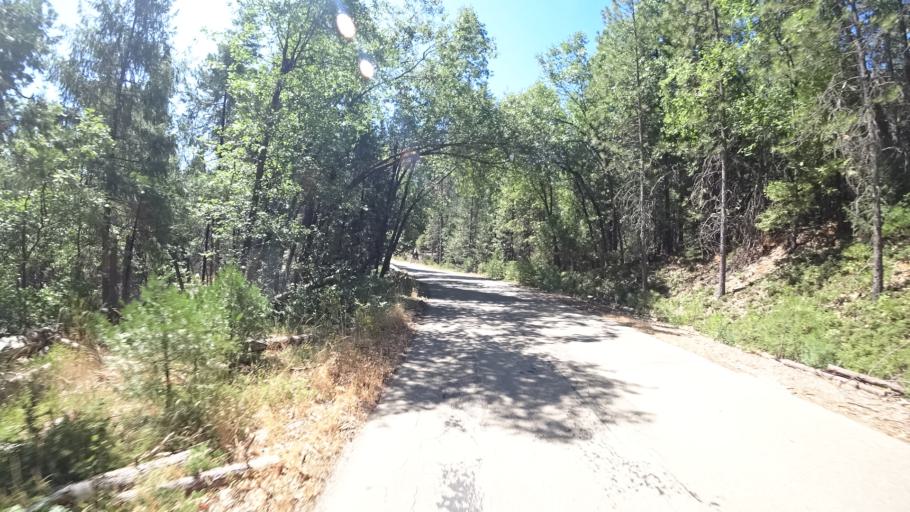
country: US
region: California
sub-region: Amador County
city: Pioneer
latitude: 38.4208
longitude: -120.4920
